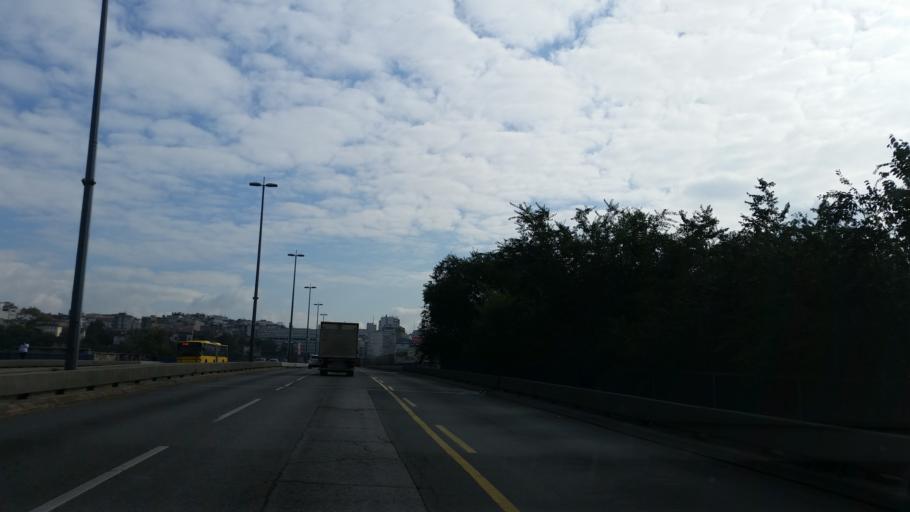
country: RS
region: Central Serbia
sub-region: Belgrade
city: Stari Grad
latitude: 44.8146
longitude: 20.4442
